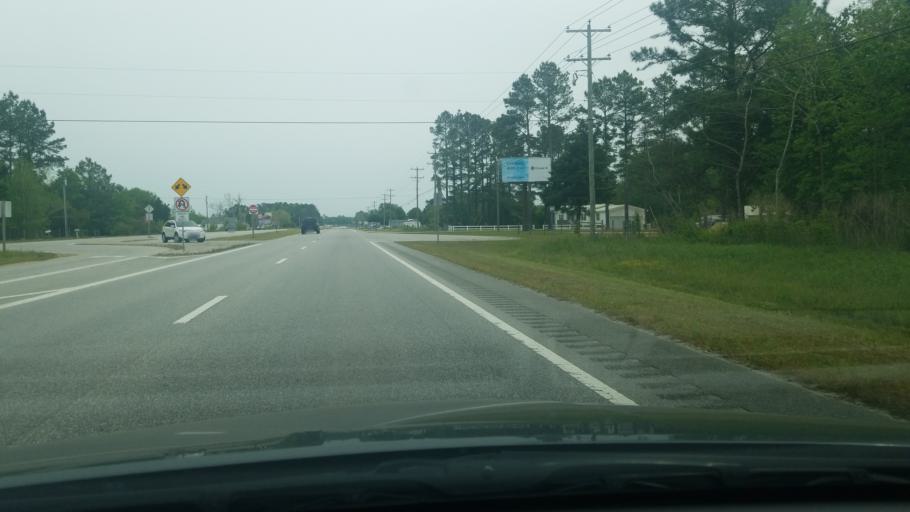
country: US
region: North Carolina
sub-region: Beaufort County
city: Washington
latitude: 35.4791
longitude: -77.1144
